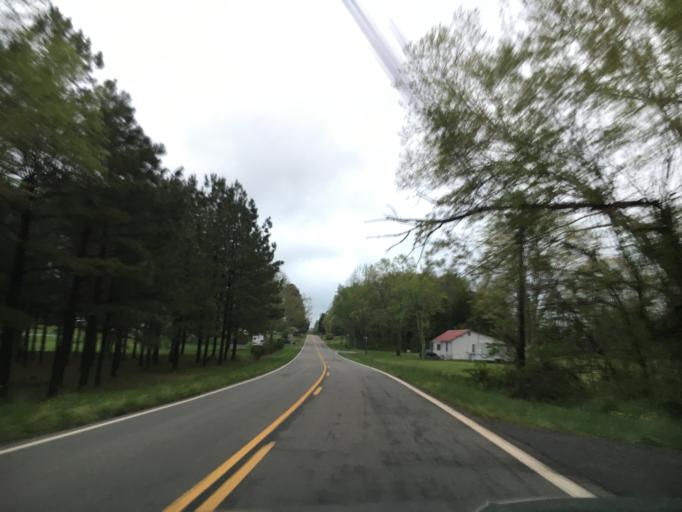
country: US
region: Virginia
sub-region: Halifax County
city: South Boston
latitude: 36.6556
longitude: -78.8768
